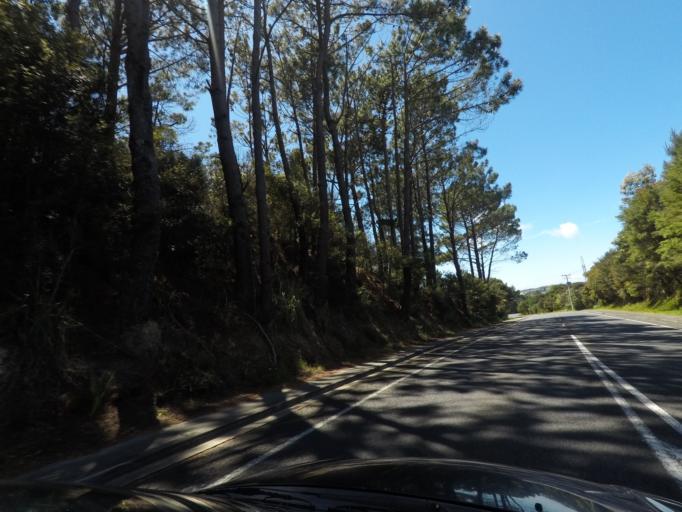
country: NZ
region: Auckland
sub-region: Auckland
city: Rothesay Bay
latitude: -36.7286
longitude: 174.6784
